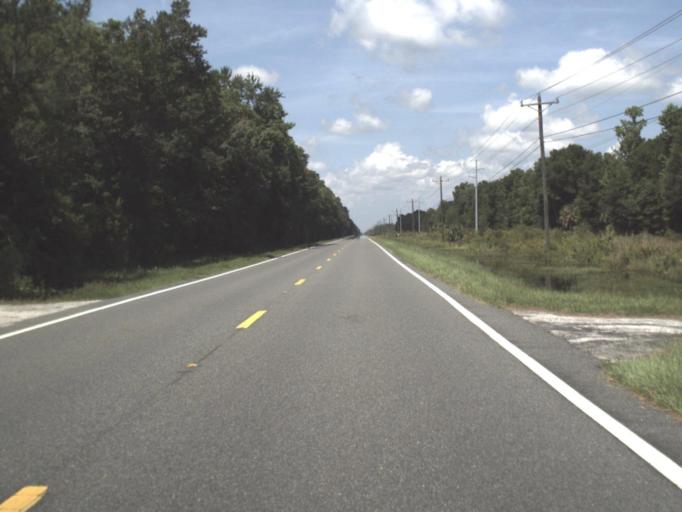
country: US
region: Florida
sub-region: Levy County
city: Chiefland
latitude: 29.3043
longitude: -82.8090
